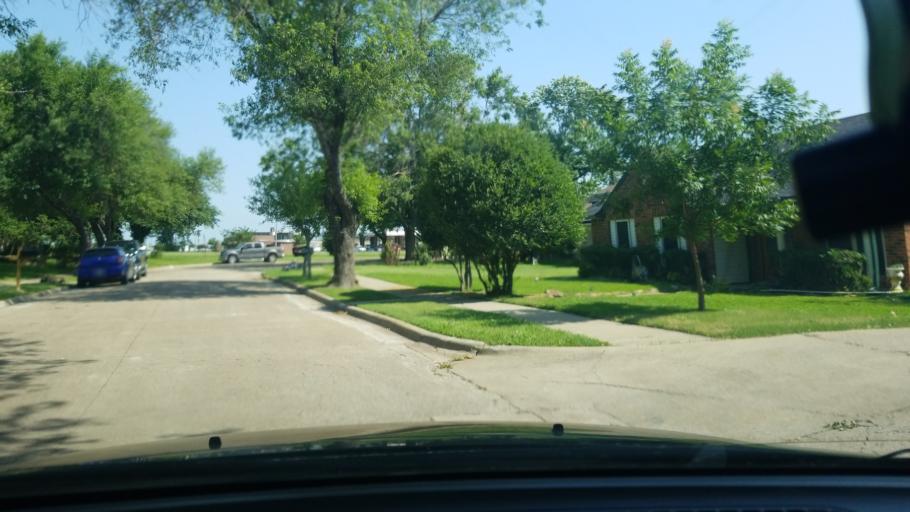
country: US
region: Texas
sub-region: Dallas County
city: Mesquite
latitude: 32.8223
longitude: -96.6226
